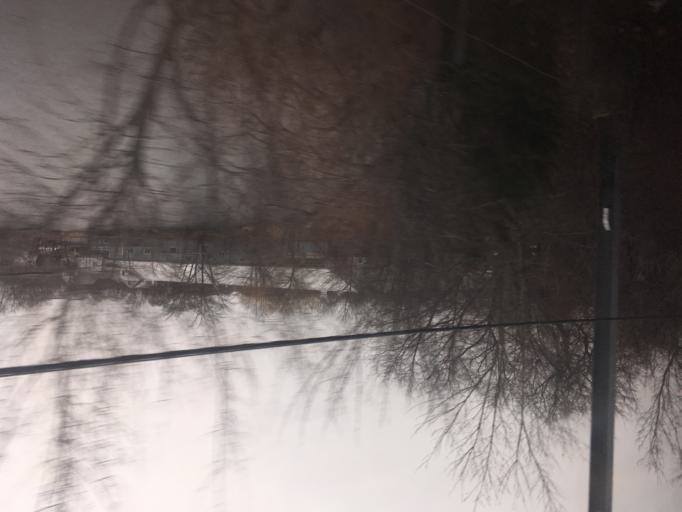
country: US
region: Massachusetts
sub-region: Norfolk County
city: Dedham
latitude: 42.2325
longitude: -71.1364
